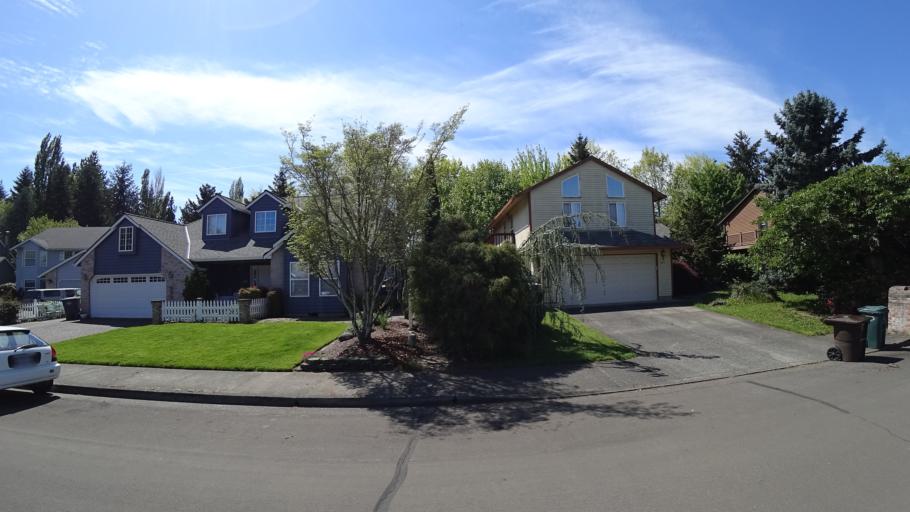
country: US
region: Oregon
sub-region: Washington County
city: Hillsboro
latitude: 45.5131
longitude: -122.9507
